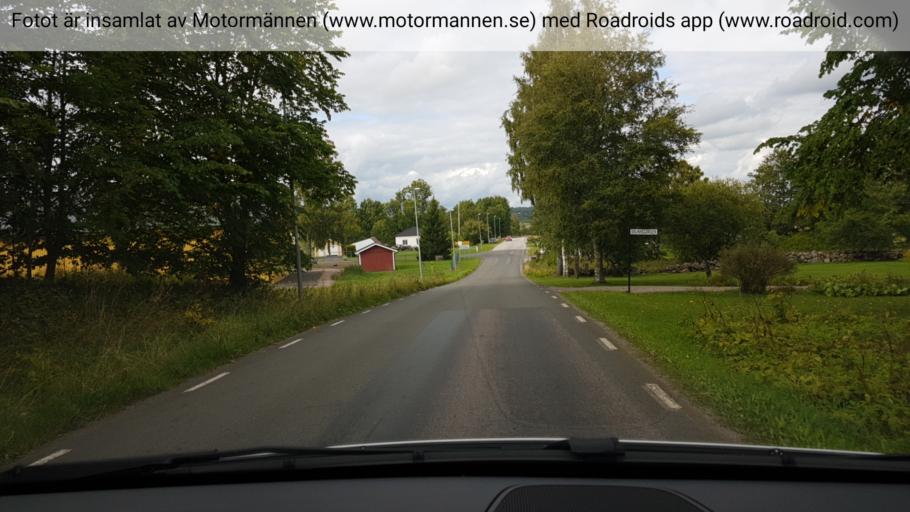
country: SE
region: Vaestra Goetaland
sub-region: Skovde Kommun
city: Skultorp
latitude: 58.2699
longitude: 13.7890
